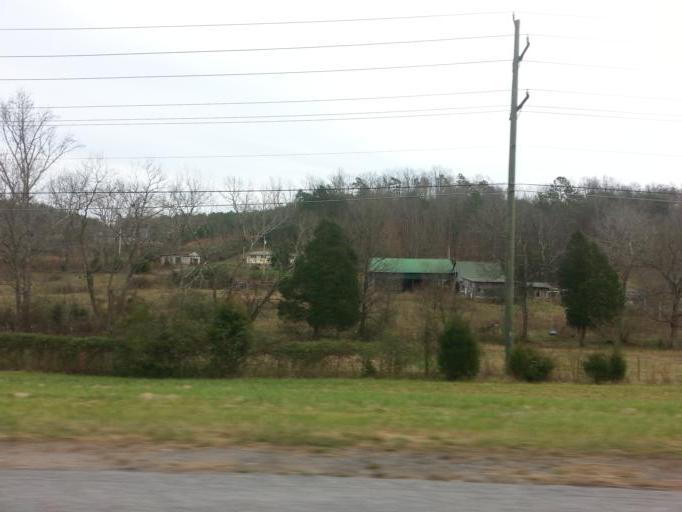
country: US
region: Tennessee
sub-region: Hamilton County
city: Sale Creek
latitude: 35.3568
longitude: -85.1215
